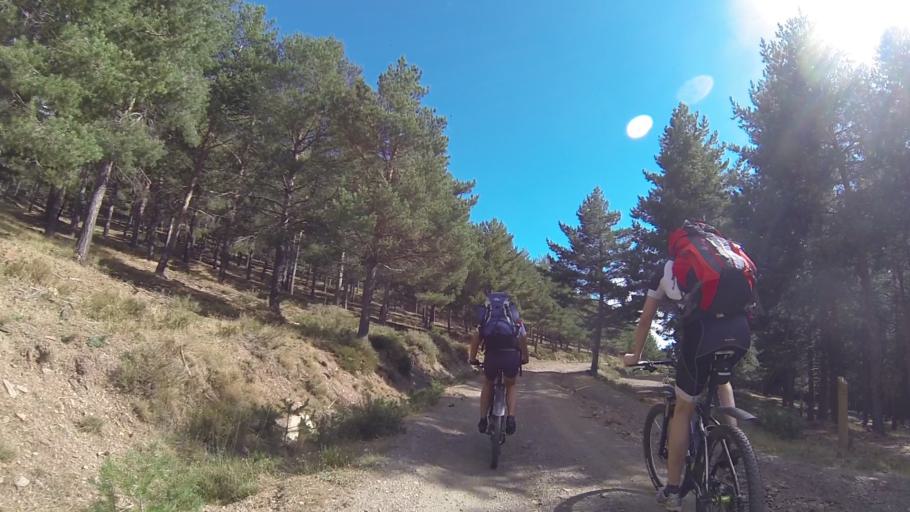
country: ES
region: Andalusia
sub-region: Provincia de Granada
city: Ferreira
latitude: 37.1128
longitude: -3.0272
